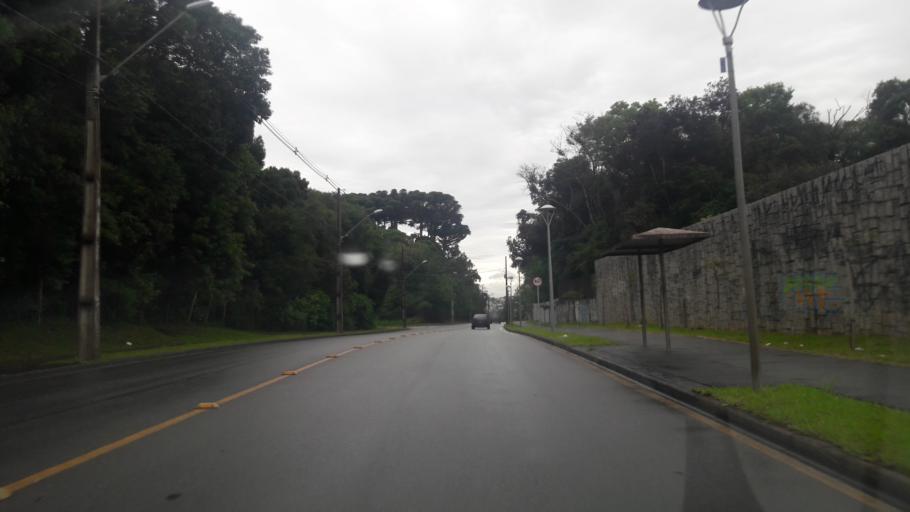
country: BR
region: Parana
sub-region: Almirante Tamandare
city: Almirante Tamandare
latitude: -25.3829
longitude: -49.3112
